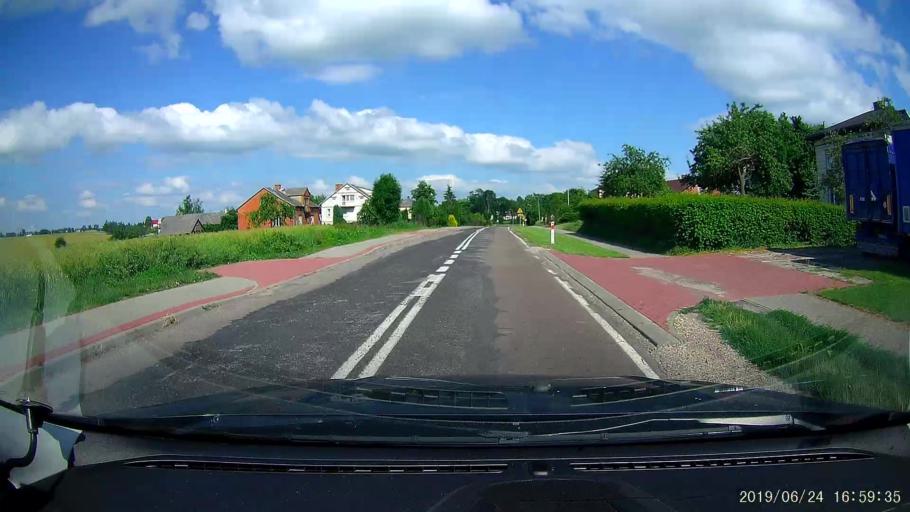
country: PL
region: Lublin Voivodeship
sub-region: Powiat tomaszowski
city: Telatyn
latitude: 50.5233
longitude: 23.9048
